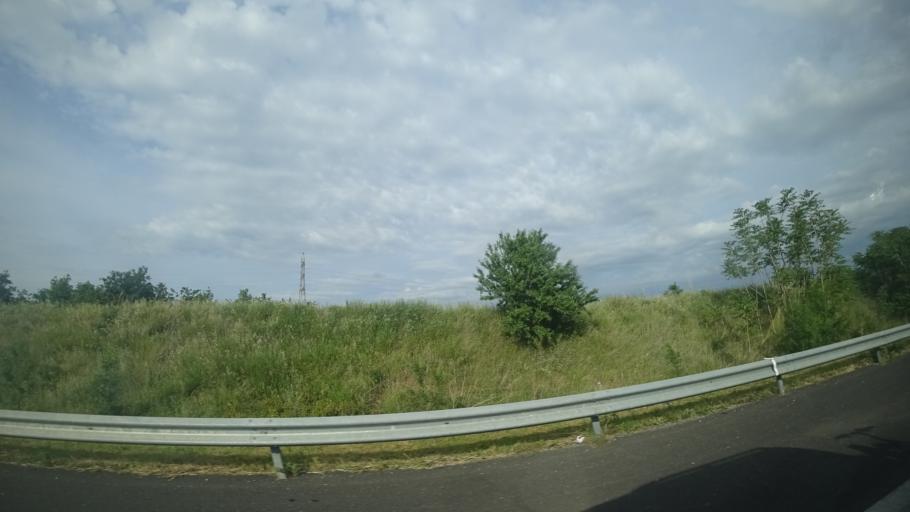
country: FR
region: Languedoc-Roussillon
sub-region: Departement de l'Herault
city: Nebian
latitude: 43.5989
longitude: 3.4628
